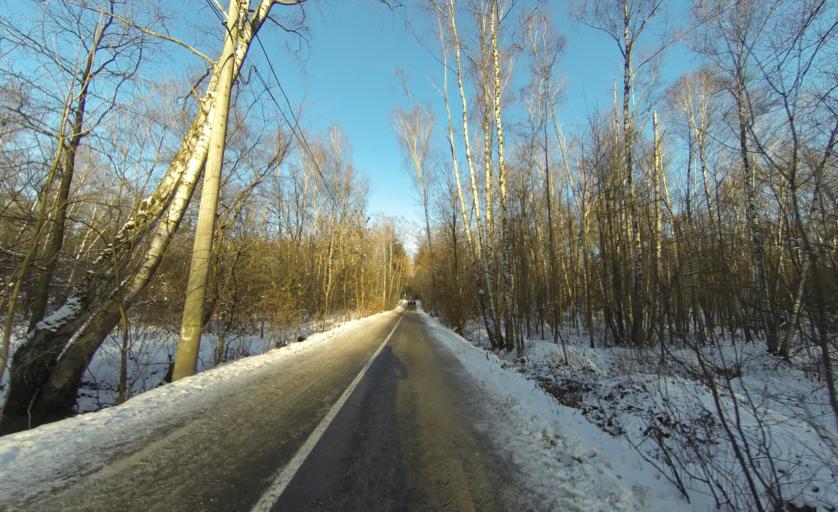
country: RU
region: Moscow
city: Sokol'niki
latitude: 55.8018
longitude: 37.6794
